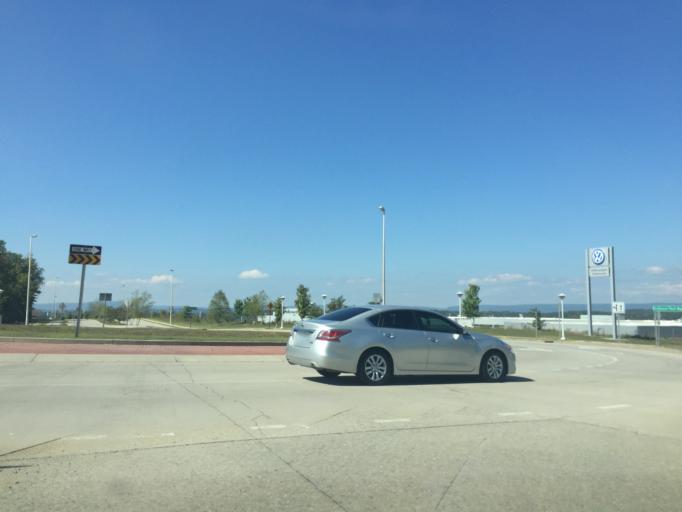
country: US
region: Tennessee
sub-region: Hamilton County
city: Harrison
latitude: 35.0766
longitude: -85.1269
